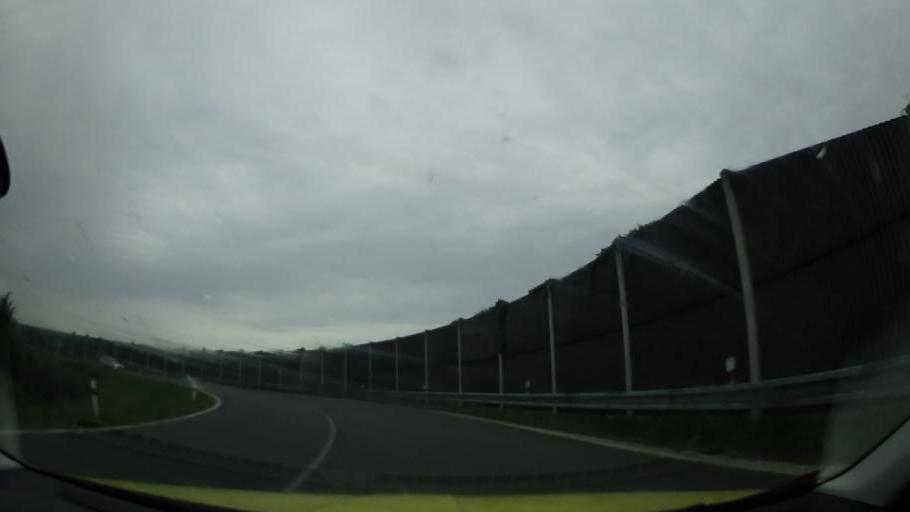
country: CZ
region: Olomoucky
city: Belotin
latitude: 49.5799
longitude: 17.7898
